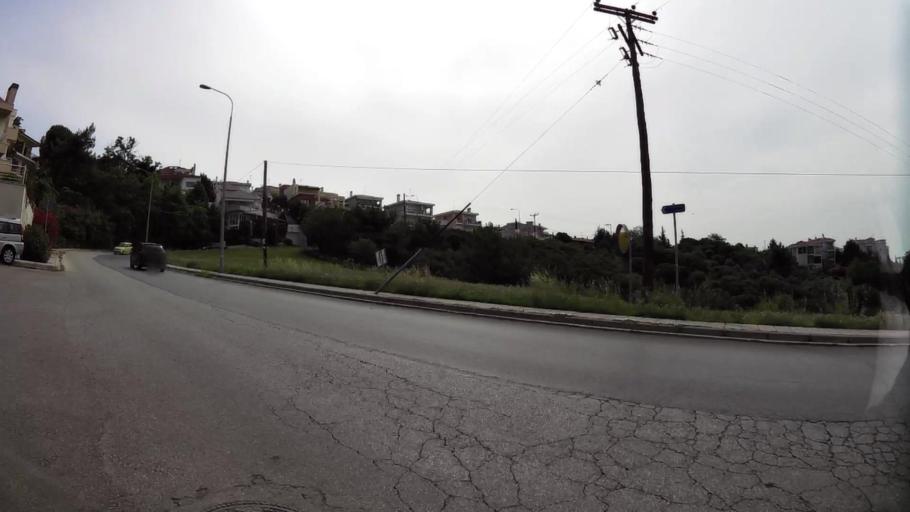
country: GR
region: Central Macedonia
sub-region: Nomos Thessalonikis
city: Panorama
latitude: 40.5778
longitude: 23.0217
